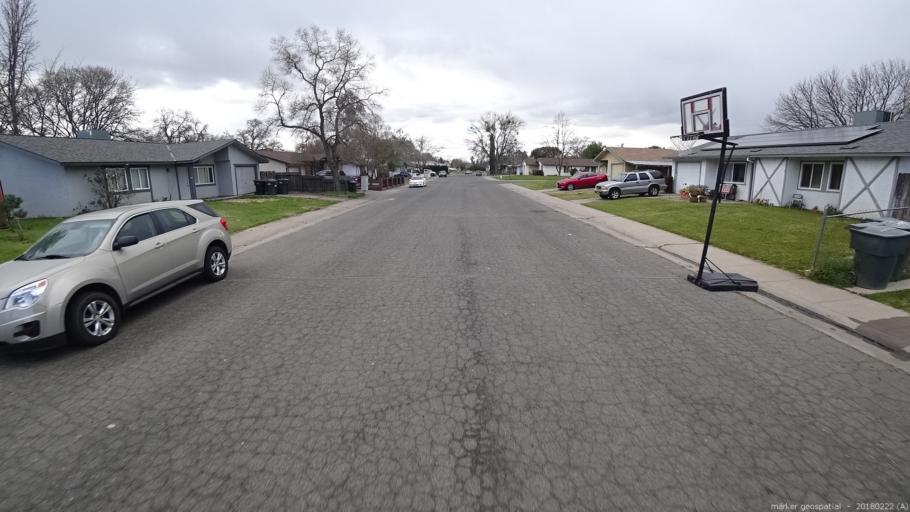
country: US
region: California
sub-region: Sacramento County
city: Rio Linda
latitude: 38.7097
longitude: -121.4121
